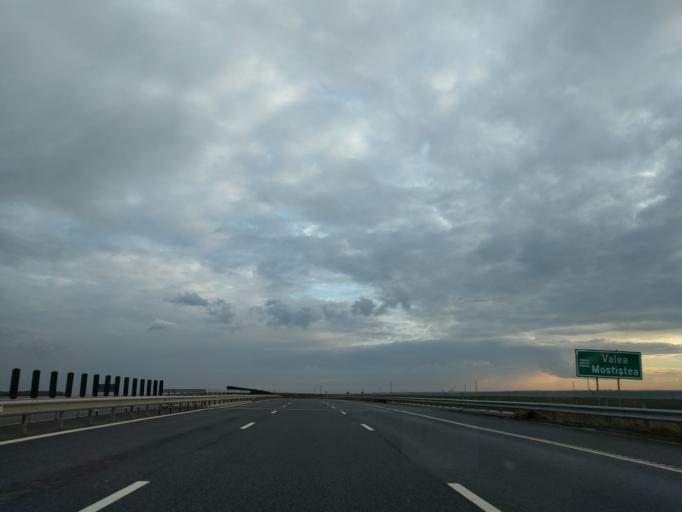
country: RO
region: Ilfov
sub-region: Comuna Moara Vlasiei
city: Caciulati
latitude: 44.6014
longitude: 26.1764
